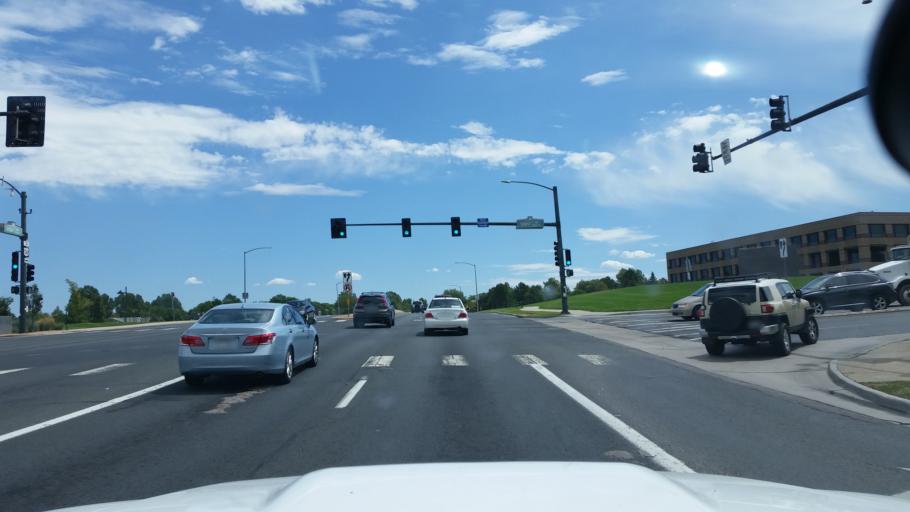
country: US
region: Colorado
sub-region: Adams County
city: Westminster
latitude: 39.8635
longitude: -105.0509
